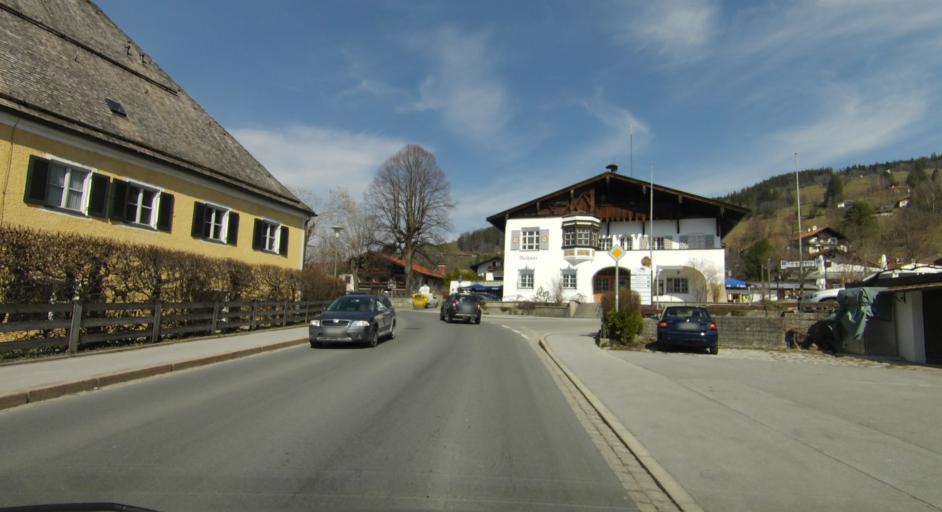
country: DE
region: Bavaria
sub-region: Upper Bavaria
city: Schliersee
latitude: 47.7339
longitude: 11.8649
